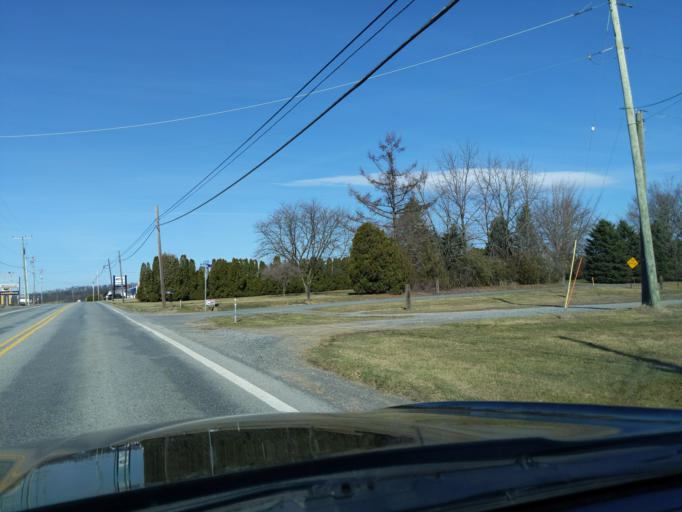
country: US
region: Pennsylvania
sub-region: Blair County
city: Martinsburg
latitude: 40.3088
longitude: -78.2882
